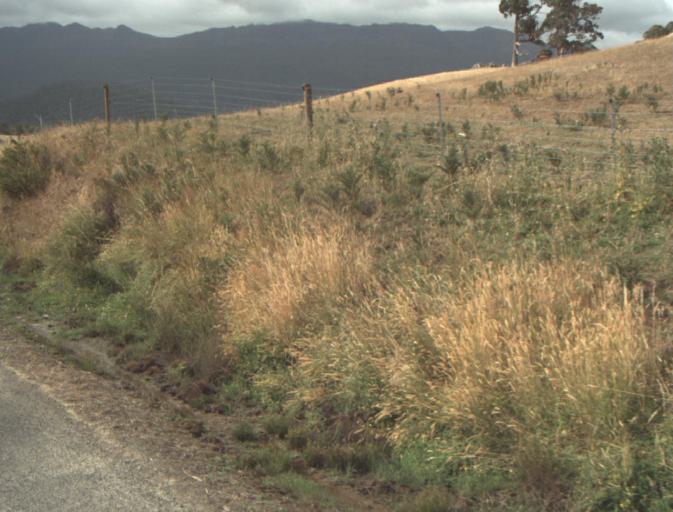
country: AU
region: Tasmania
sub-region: Dorset
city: Scottsdale
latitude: -41.4495
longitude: 147.5888
